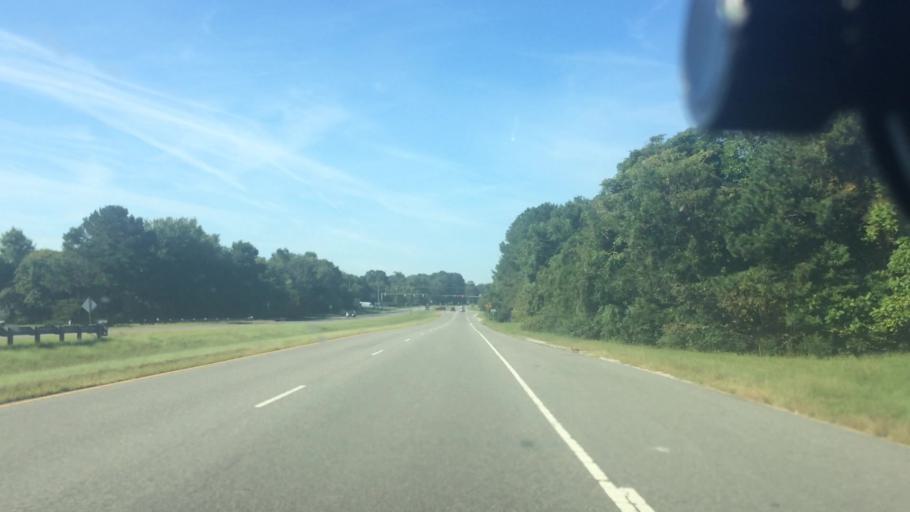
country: US
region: Virginia
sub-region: James City County
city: Williamsburg
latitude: 37.3843
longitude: -76.7638
